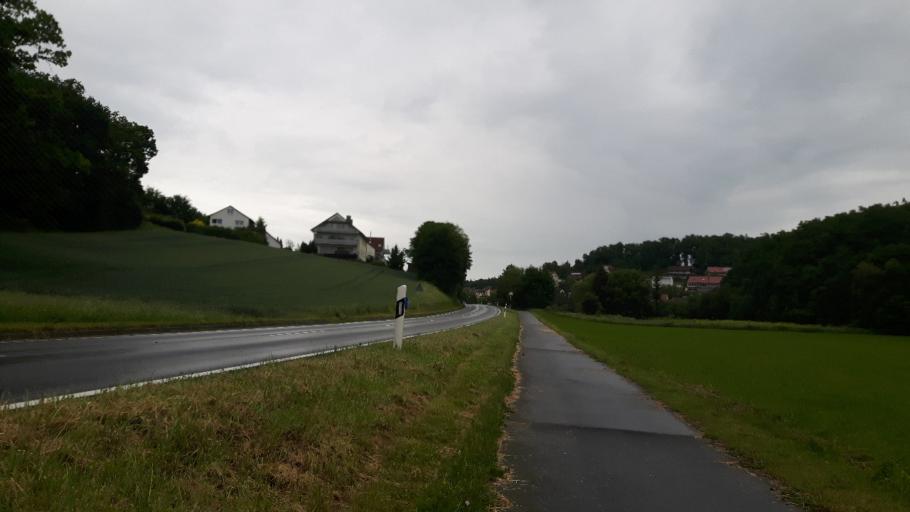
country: DE
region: Bavaria
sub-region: Regierungsbezirk Unterfranken
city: Uchtelhausen
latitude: 50.0889
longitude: 10.2470
